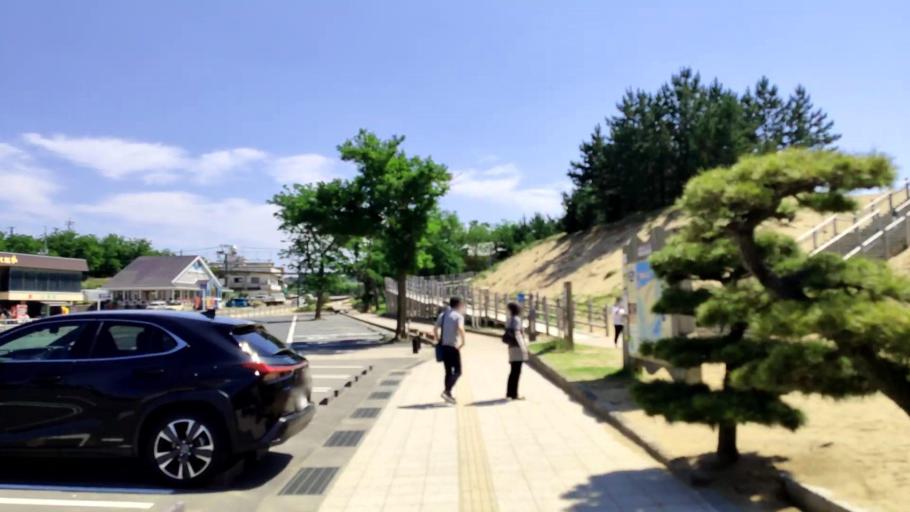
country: JP
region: Tottori
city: Tottori
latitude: 35.5437
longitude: 134.2367
